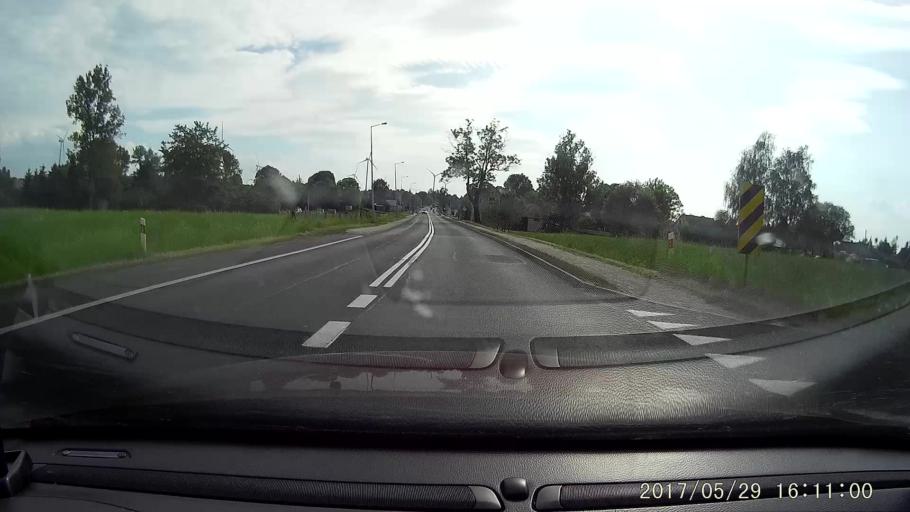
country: PL
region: Lower Silesian Voivodeship
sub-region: Powiat zgorzelecki
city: Lagow
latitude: 51.1975
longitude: 15.0886
